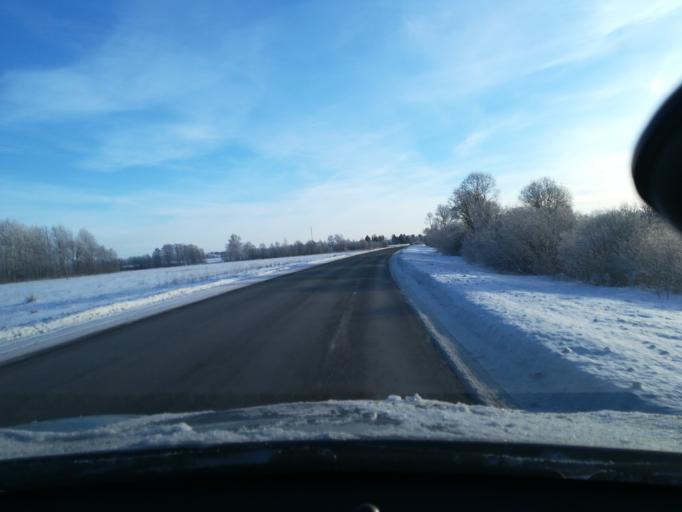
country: EE
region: Harju
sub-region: Harku vald
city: Tabasalu
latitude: 59.3731
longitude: 24.4727
